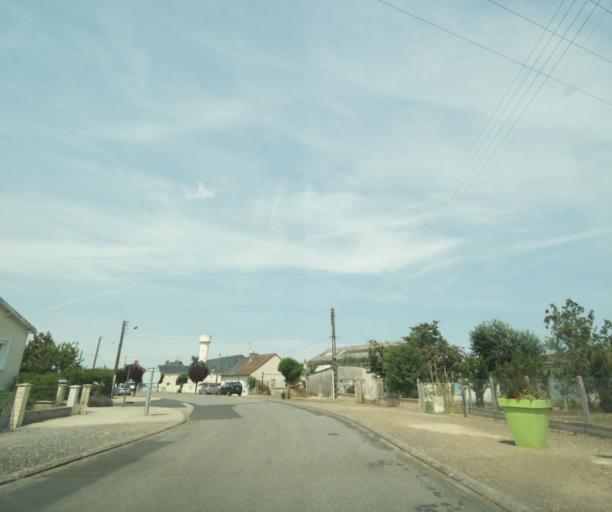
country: FR
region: Centre
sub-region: Departement d'Indre-et-Loire
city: La Celle-Saint-Avant
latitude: 46.9992
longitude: 0.5998
